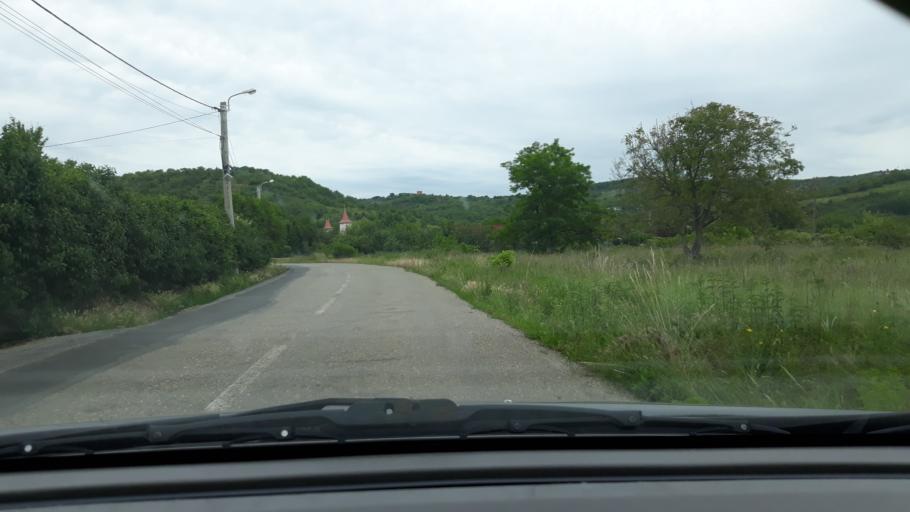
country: RO
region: Bihor
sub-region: Comuna Osorheiu
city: Alparea
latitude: 47.0562
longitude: 22.0017
